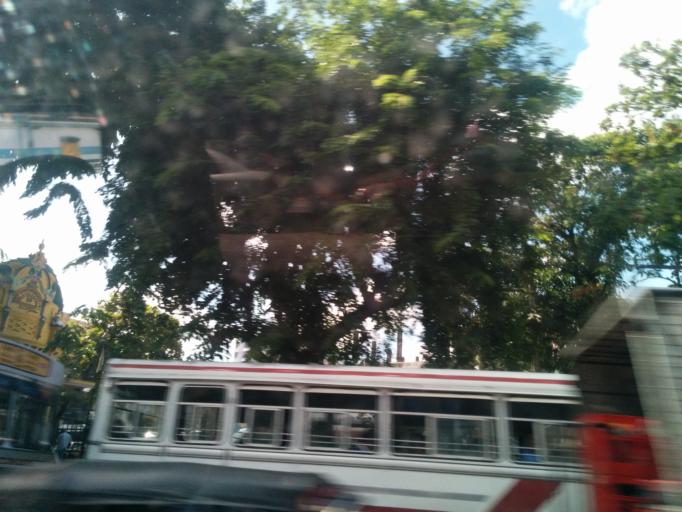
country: LK
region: Western
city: Kolonnawa
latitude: 6.9447
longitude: 79.8669
